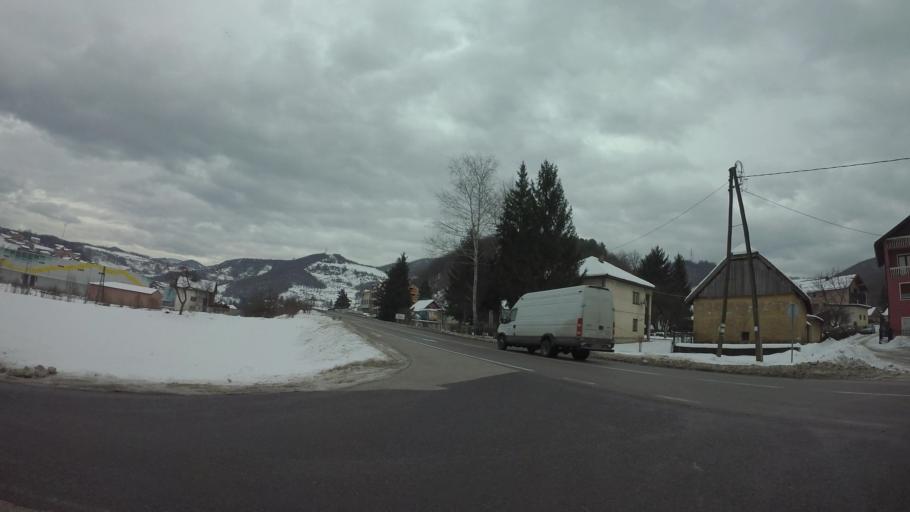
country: BA
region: Federation of Bosnia and Herzegovina
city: Vogosca
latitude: 43.8851
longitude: 18.3205
